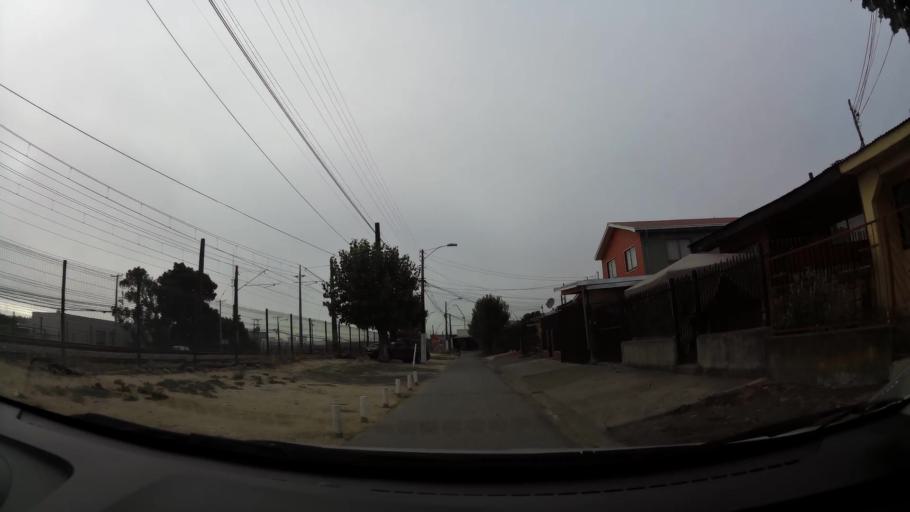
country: CL
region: Biobio
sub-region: Provincia de Concepcion
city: Concepcion
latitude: -36.8001
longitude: -73.0800
